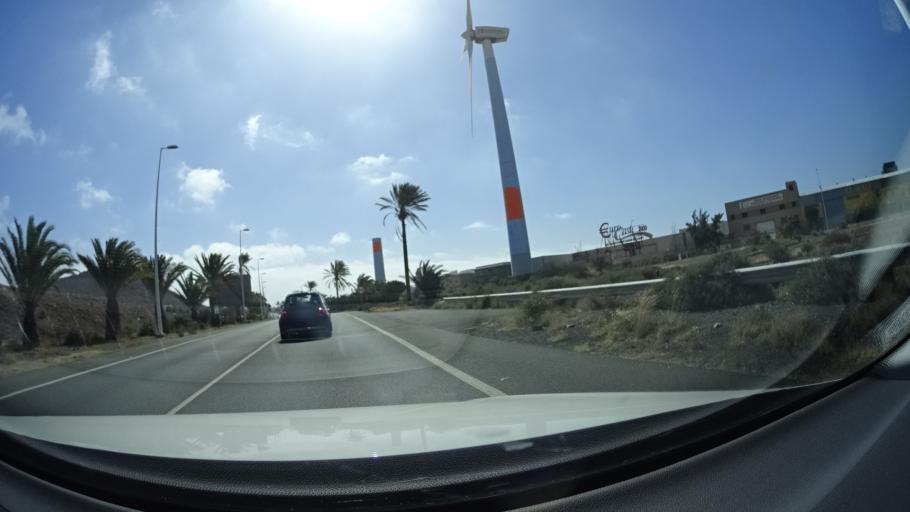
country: ES
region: Canary Islands
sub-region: Provincia de Las Palmas
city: Cruce de Arinaga
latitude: 27.8702
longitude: -15.4175
